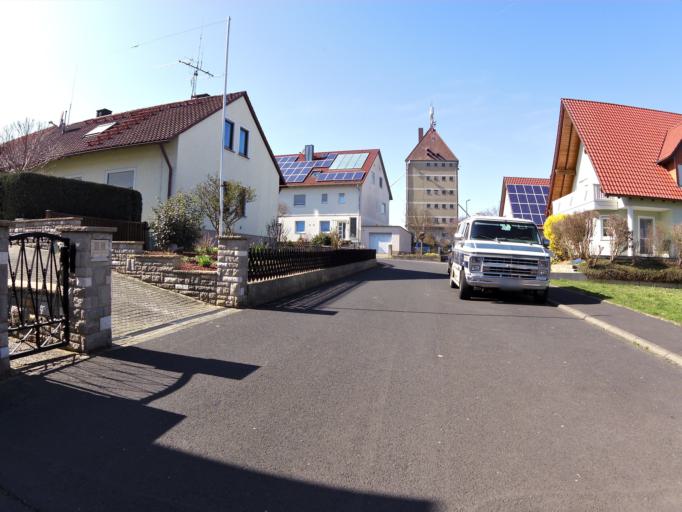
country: DE
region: Bavaria
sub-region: Regierungsbezirk Unterfranken
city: Prosselsheim
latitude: 49.8632
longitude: 10.1248
